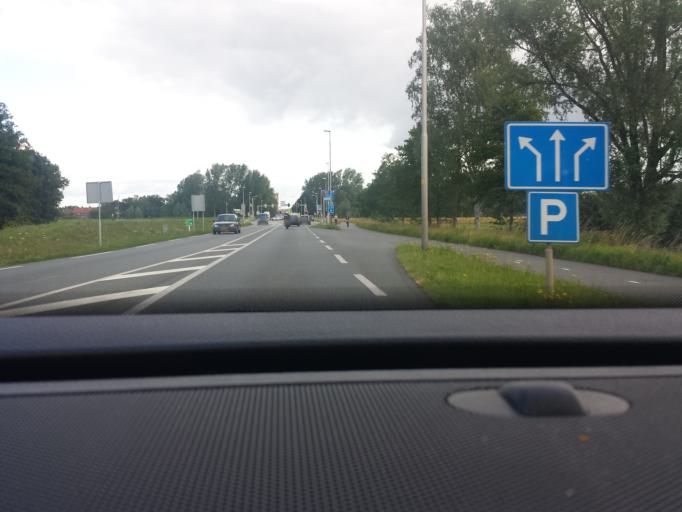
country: NL
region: Gelderland
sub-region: Gemeente Zutphen
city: Warnsveld
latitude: 52.1431
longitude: 6.2165
